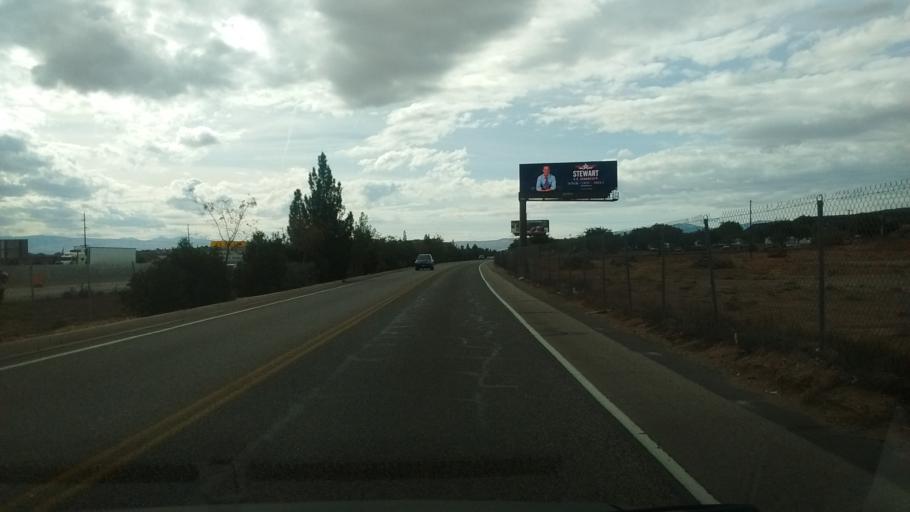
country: US
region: Utah
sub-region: Washington County
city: Washington
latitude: 37.1243
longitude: -113.5335
